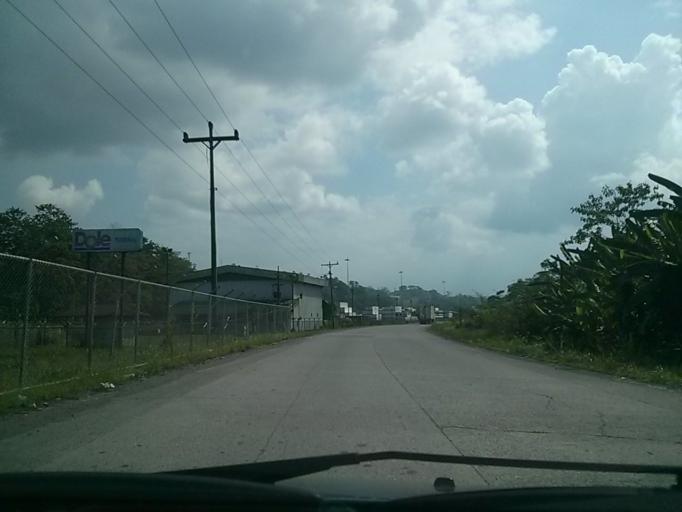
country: CR
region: Limon
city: Limon
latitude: 9.9974
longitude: -83.0775
